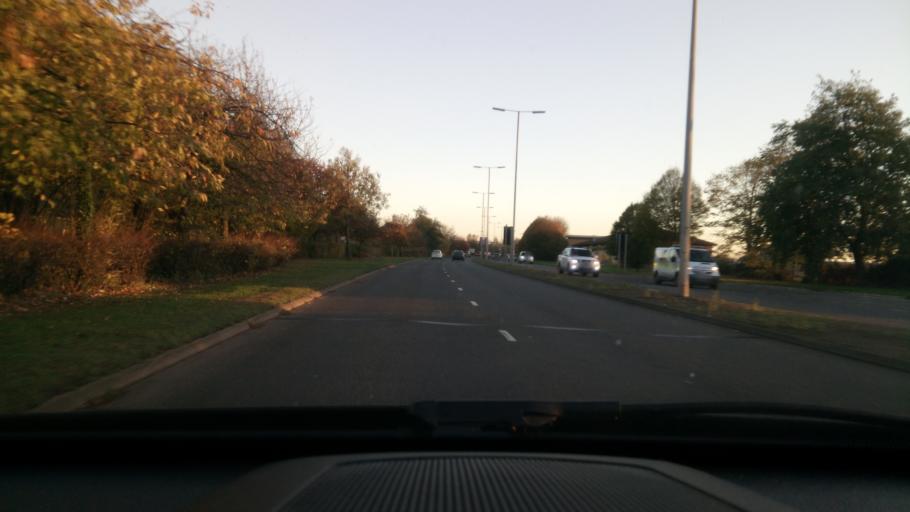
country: GB
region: England
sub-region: Peterborough
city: Peterborough
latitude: 52.5942
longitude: -0.2588
